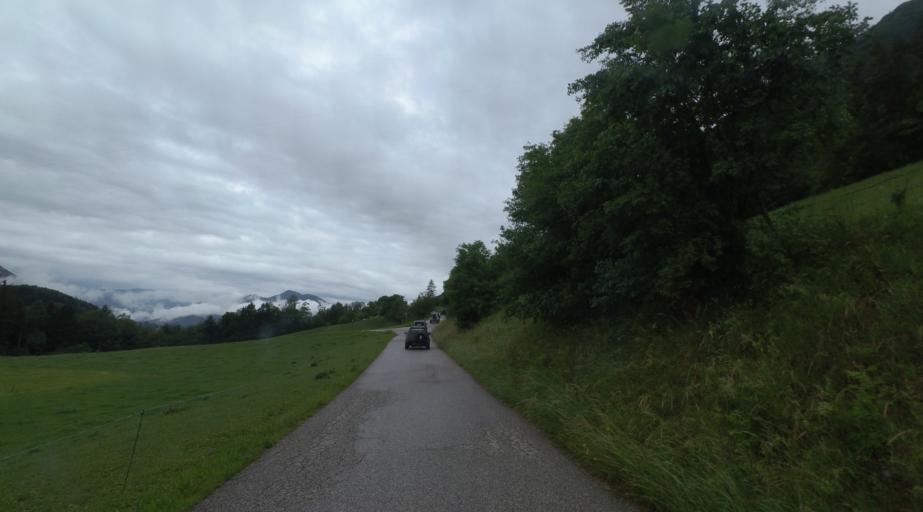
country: AT
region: Upper Austria
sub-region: Politischer Bezirk Steyr-Land
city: Ternberg
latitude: 47.8945
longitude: 14.2930
